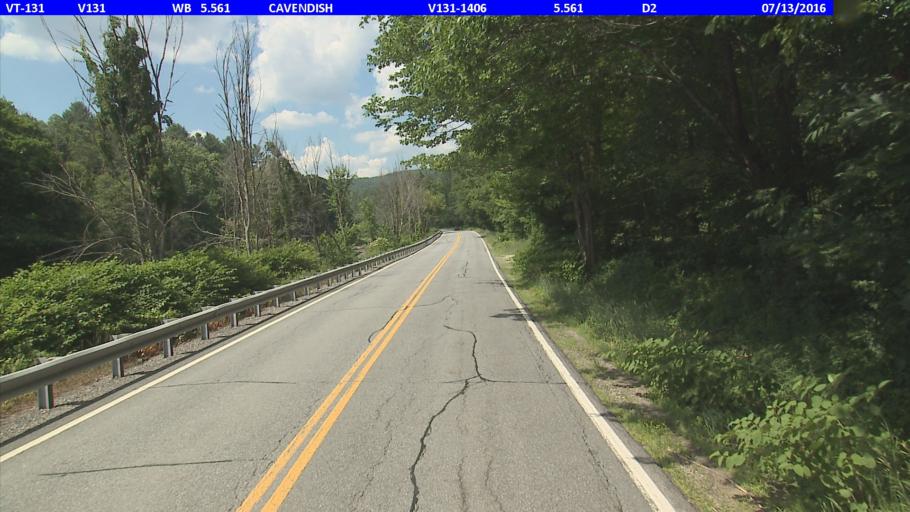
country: US
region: Vermont
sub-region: Windsor County
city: Springfield
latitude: 43.3953
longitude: -72.5680
